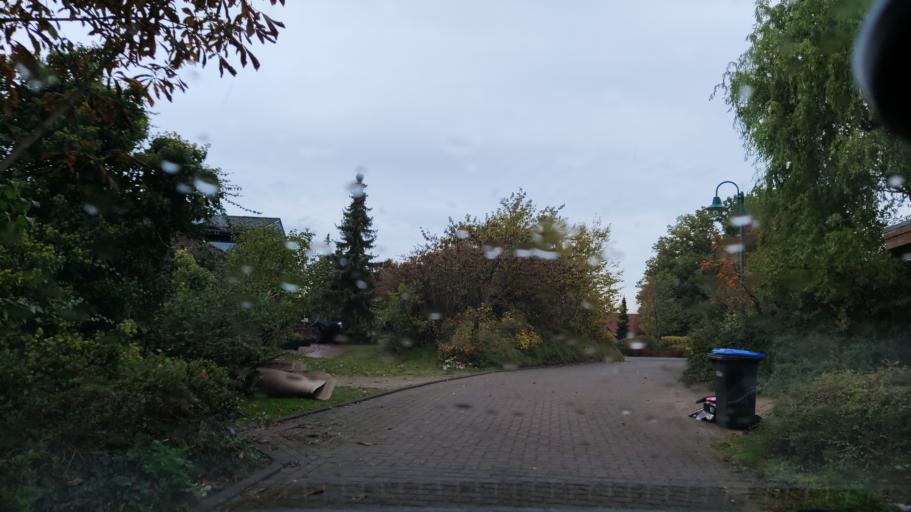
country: DE
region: Lower Saxony
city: Deutsch Evern
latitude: 53.2018
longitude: 10.4412
